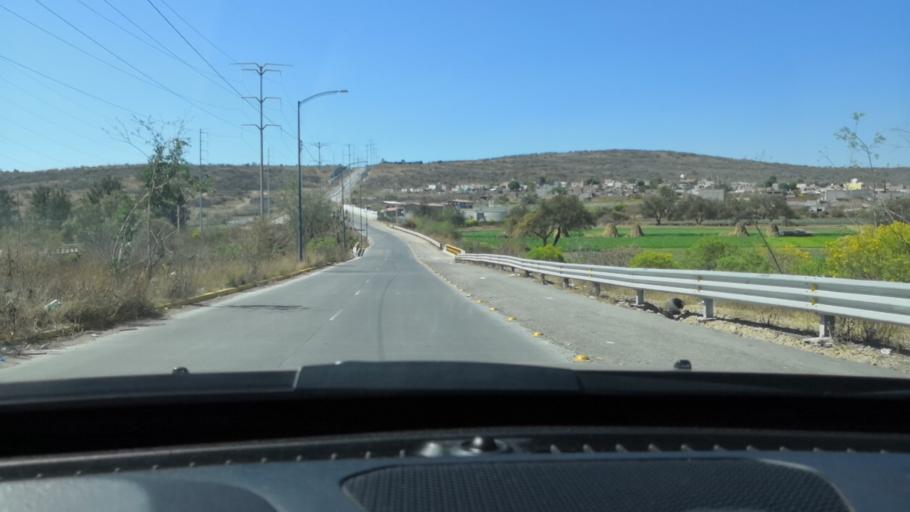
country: MX
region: Guanajuato
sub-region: Leon
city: Centro Familiar la Soledad
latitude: 21.1258
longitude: -101.7366
